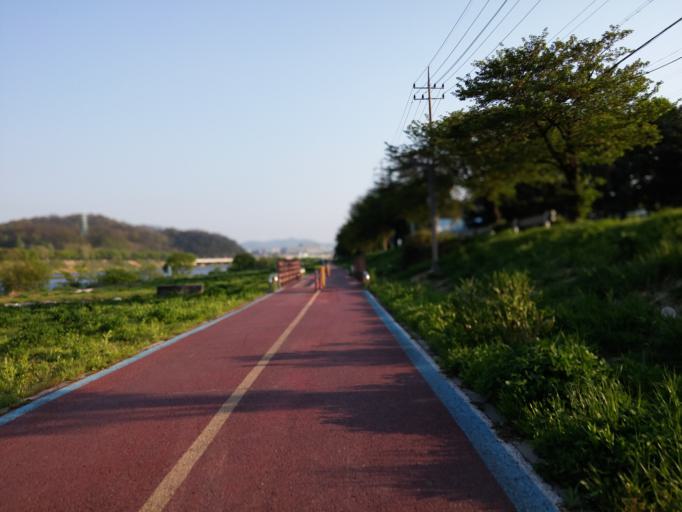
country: KR
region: Daejeon
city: Songgang-dong
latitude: 36.3905
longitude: 127.4099
